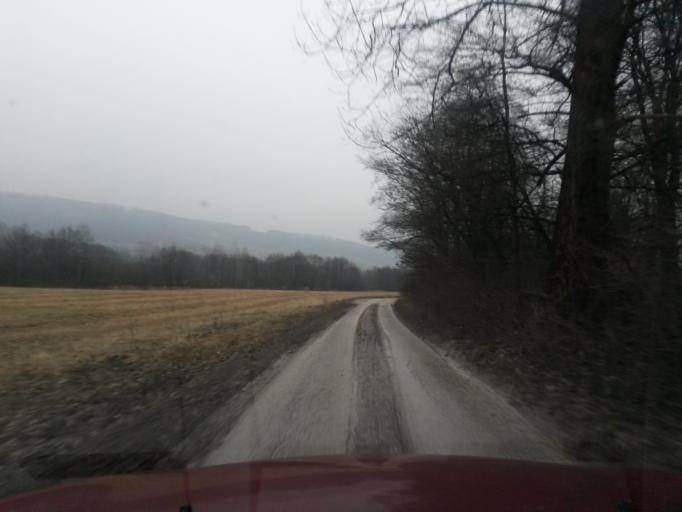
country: SK
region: Kosicky
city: Roznava
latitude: 48.6950
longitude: 20.5035
